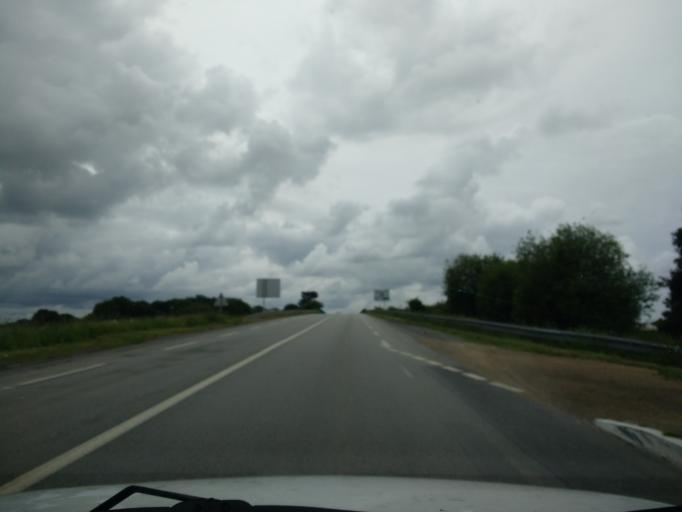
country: FR
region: Brittany
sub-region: Departement du Morbihan
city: Peaule
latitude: 47.5380
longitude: -2.3974
